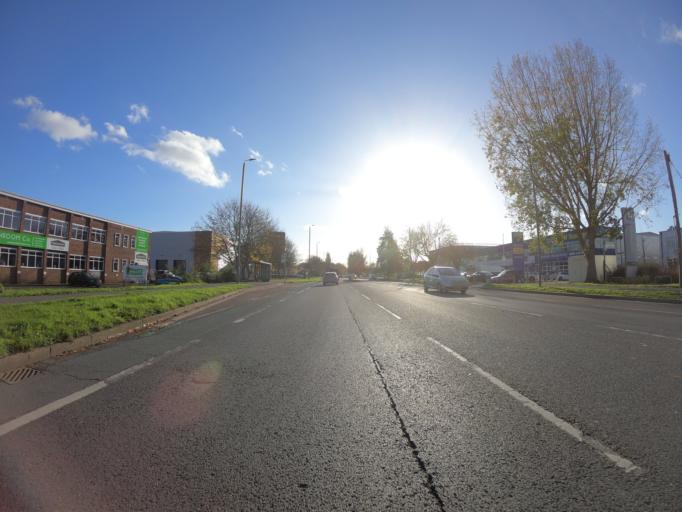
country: GB
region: England
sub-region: Greater London
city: Orpington
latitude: 51.3908
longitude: 0.1105
